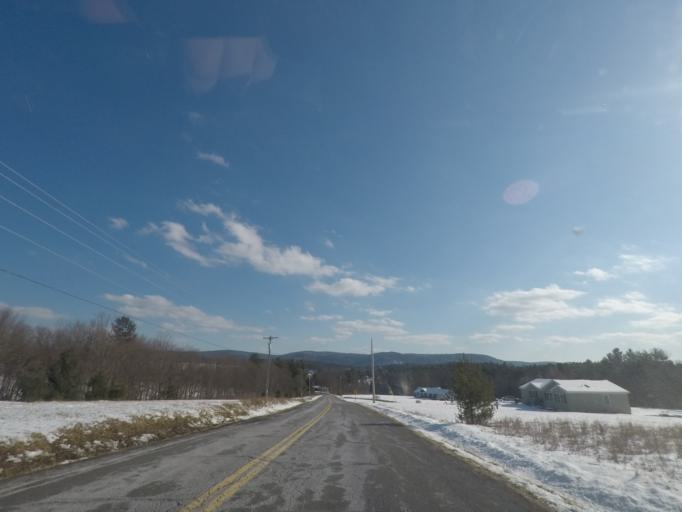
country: US
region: New York
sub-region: Rensselaer County
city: Hoosick Falls
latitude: 42.8443
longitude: -73.4888
